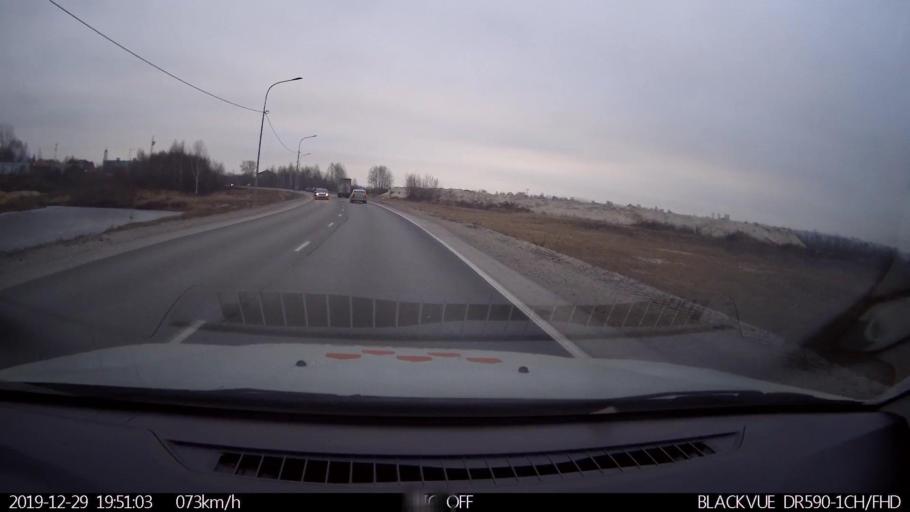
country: RU
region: Nizjnij Novgorod
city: Bor
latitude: 56.3622
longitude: 44.0344
